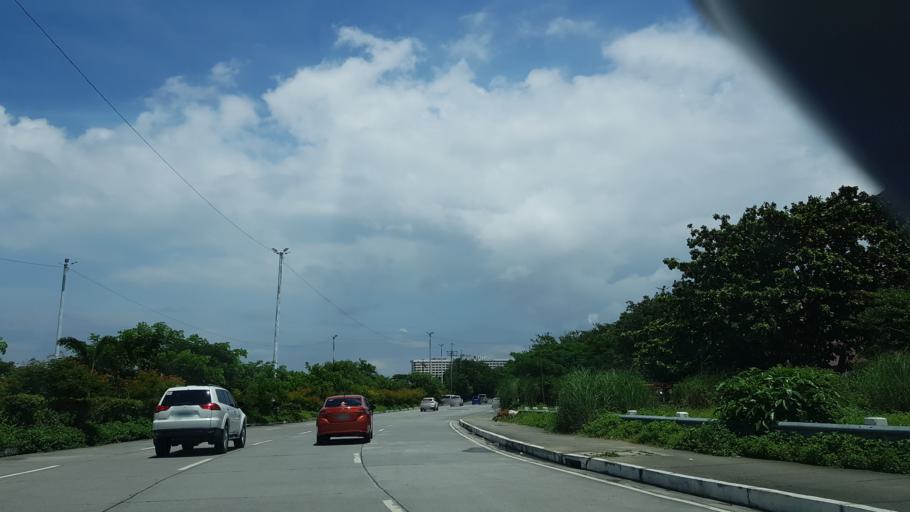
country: PH
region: Metro Manila
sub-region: City of Manila
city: Port Area
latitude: 14.5444
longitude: 120.9826
